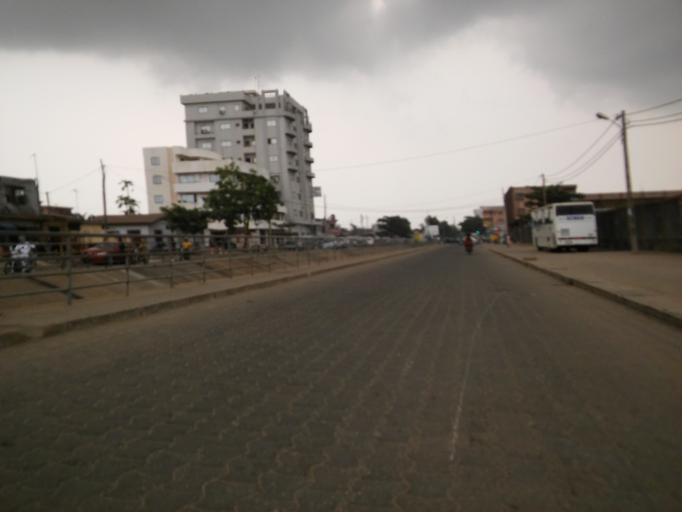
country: BJ
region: Littoral
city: Cotonou
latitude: 6.3757
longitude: 2.4151
